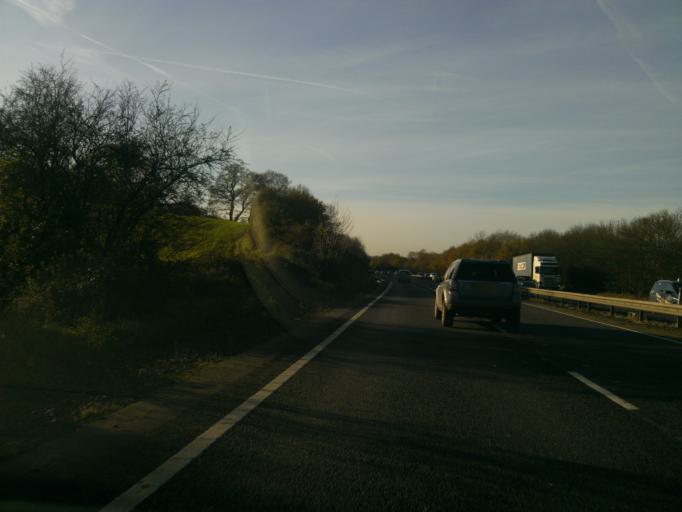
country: GB
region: England
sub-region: Essex
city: Great Horkesley
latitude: 51.9168
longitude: 0.8760
